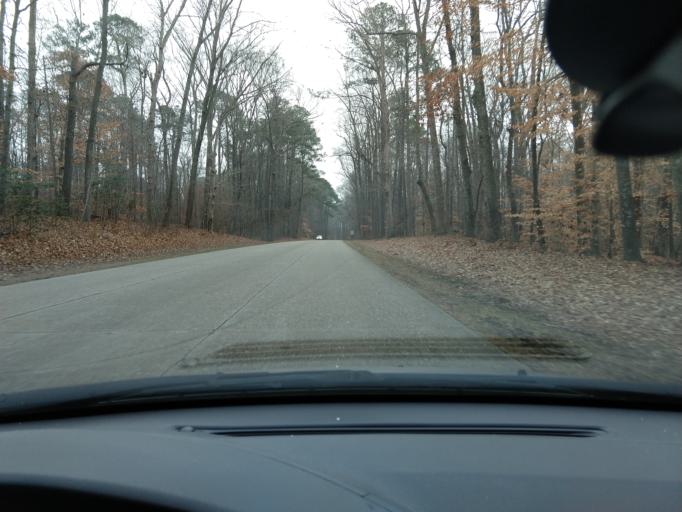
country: US
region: Virginia
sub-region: City of Williamsburg
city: Williamsburg
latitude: 37.2770
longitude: -76.6170
